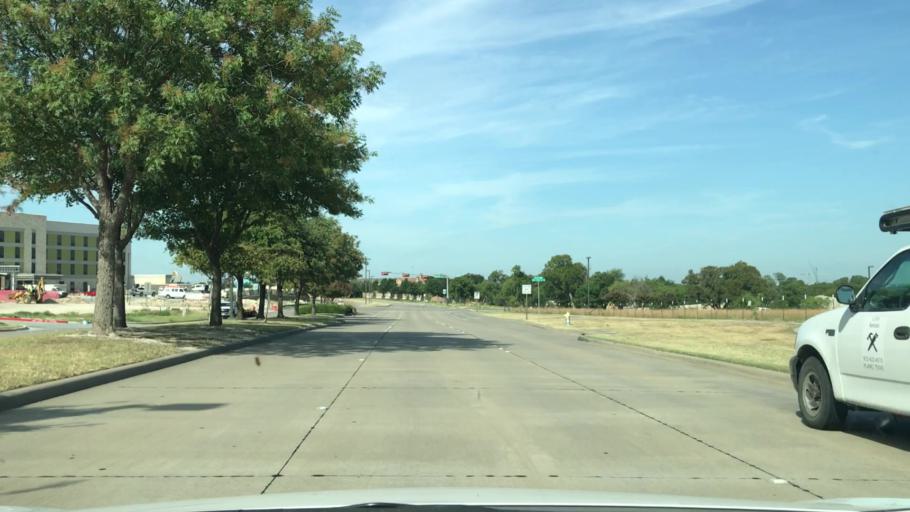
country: US
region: Texas
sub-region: Denton County
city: The Colony
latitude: 33.0714
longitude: -96.8333
